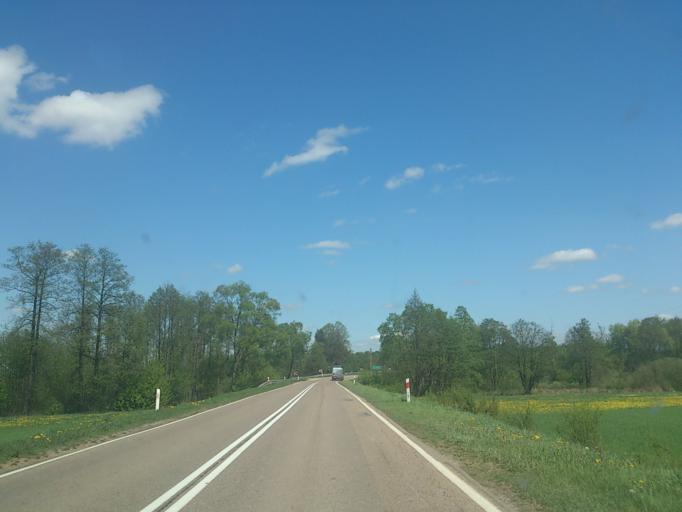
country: PL
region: Podlasie
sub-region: Powiat lomzynski
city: Wizna
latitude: 53.2079
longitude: 22.4912
